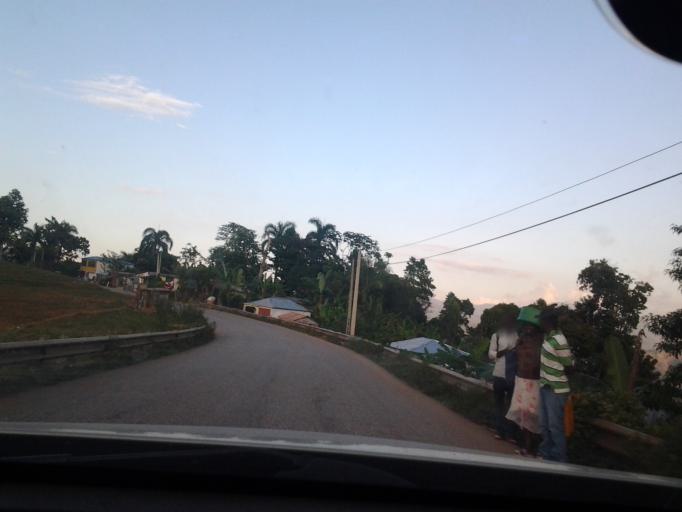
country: HT
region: Sud-Est
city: Jacmel
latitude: 18.3700
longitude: -72.5837
